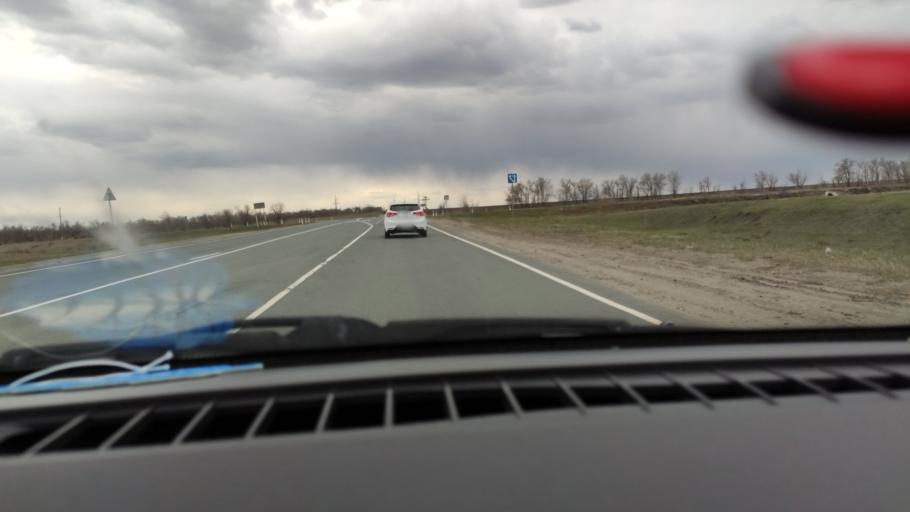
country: RU
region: Saratov
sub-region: Saratovskiy Rayon
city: Saratov
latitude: 51.7514
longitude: 46.0605
